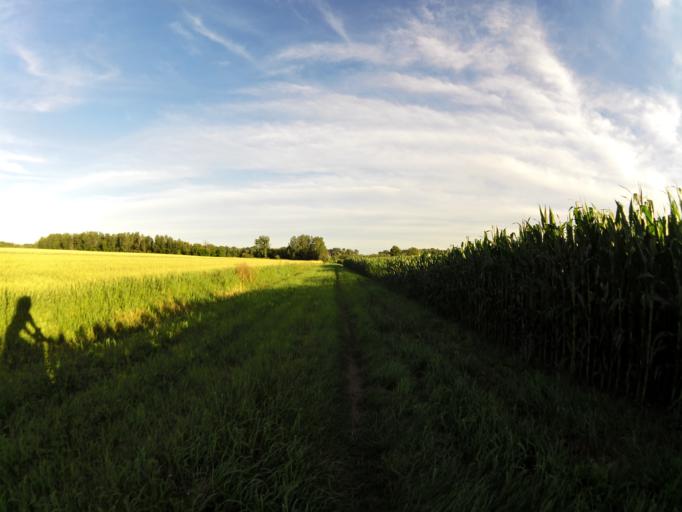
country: CA
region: Ontario
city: Ottawa
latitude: 45.4154
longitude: -75.5906
